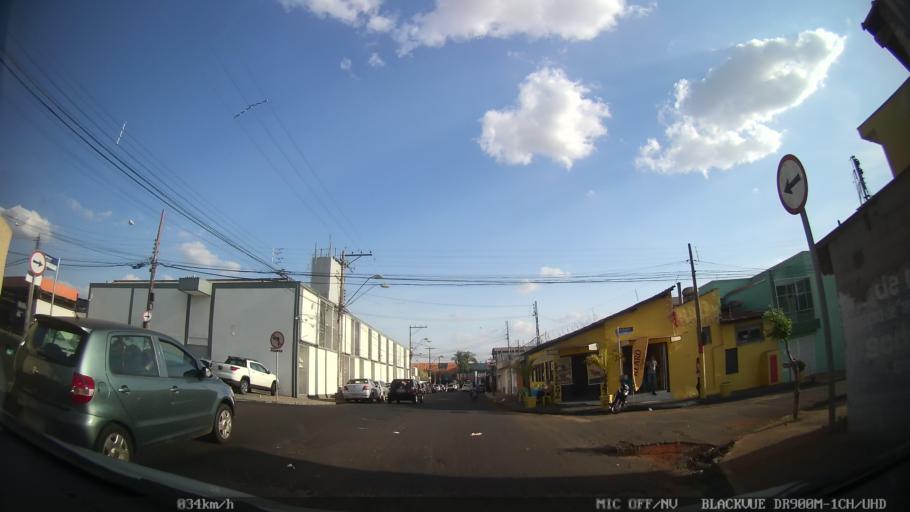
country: BR
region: Sao Paulo
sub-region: Ribeirao Preto
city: Ribeirao Preto
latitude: -21.1542
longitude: -47.8062
